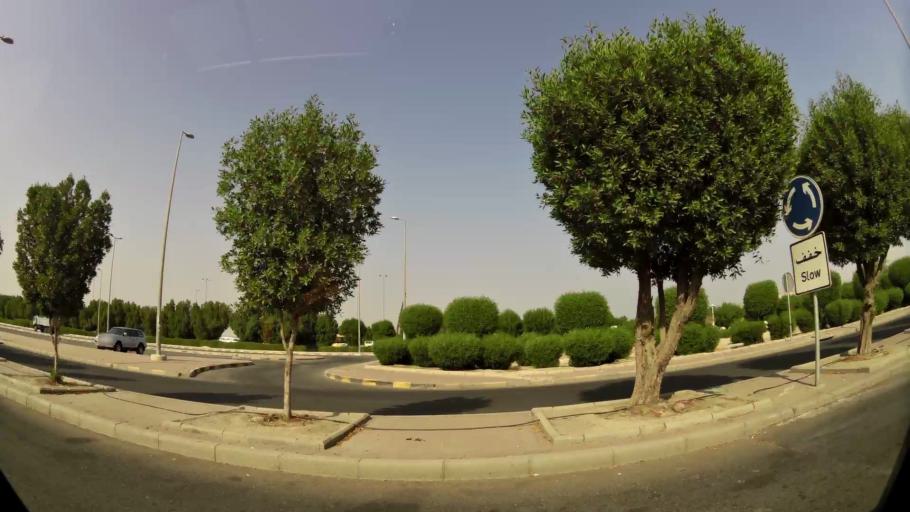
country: KW
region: Muhafazat al Jahra'
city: Al Jahra'
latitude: 29.3466
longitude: 47.6980
